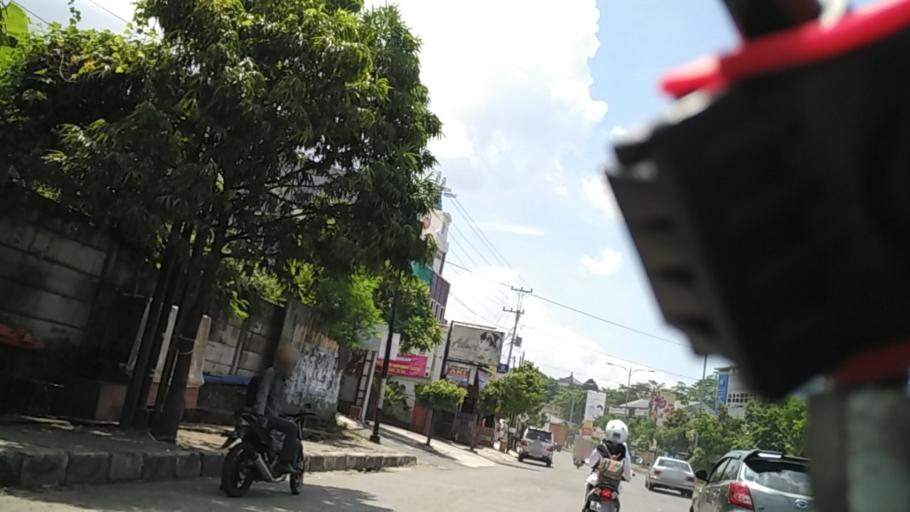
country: ID
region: Central Java
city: Semarang
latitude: -6.9885
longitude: 110.3583
